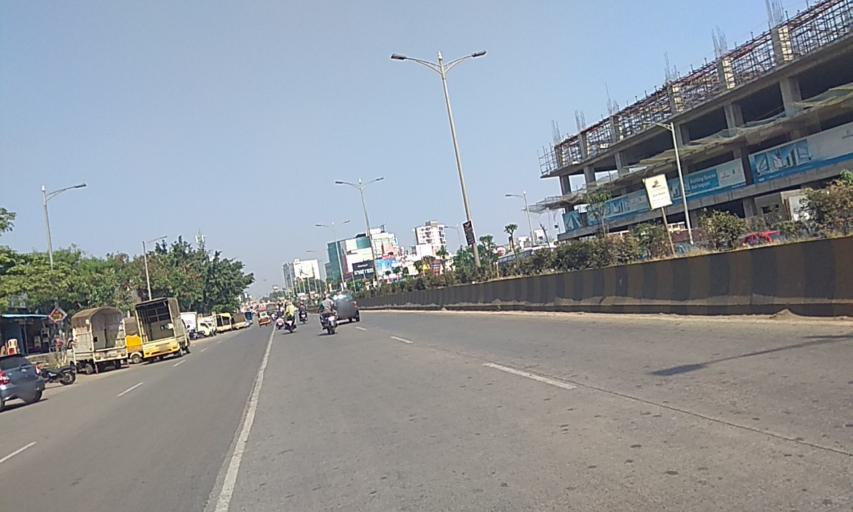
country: IN
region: Maharashtra
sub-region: Pune Division
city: Lohogaon
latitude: 18.5482
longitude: 73.9365
